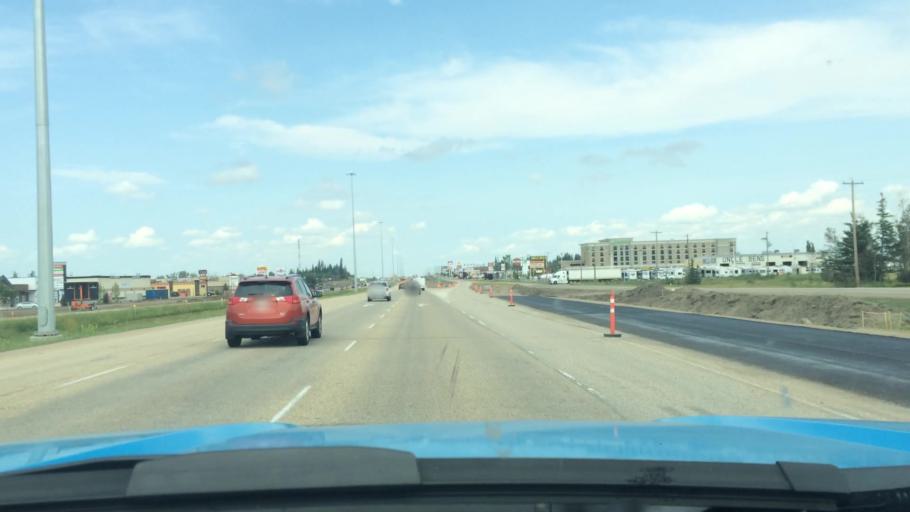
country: CA
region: Alberta
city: Red Deer
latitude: 52.2099
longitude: -113.8137
